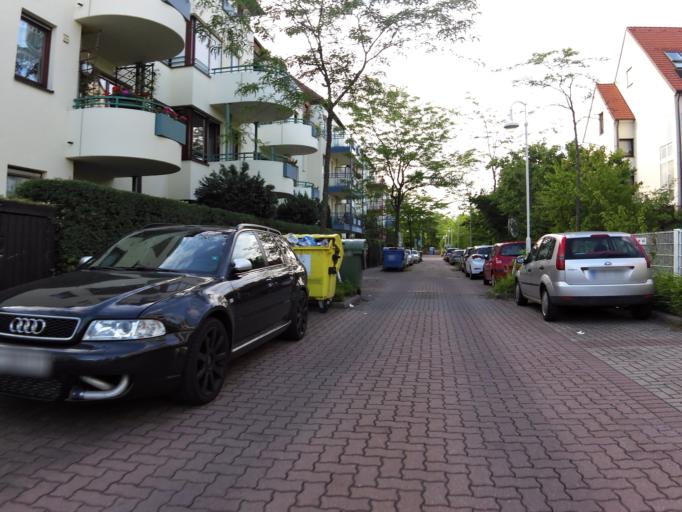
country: DE
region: Saxony
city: Taucha
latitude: 51.3272
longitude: 12.4435
